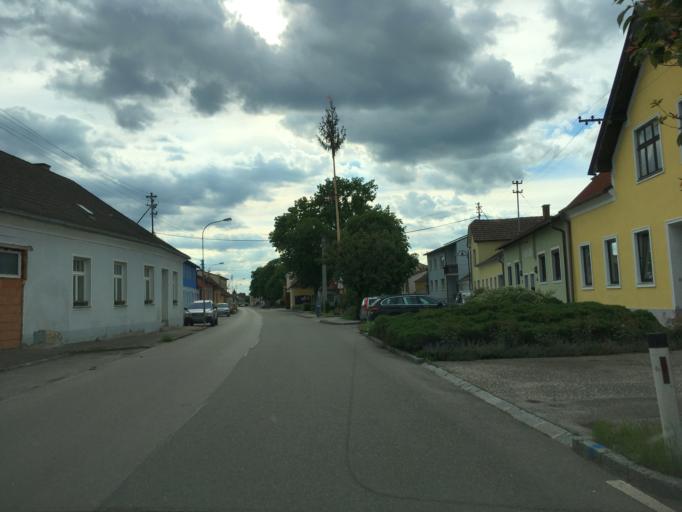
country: AT
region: Lower Austria
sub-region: Politischer Bezirk Tulln
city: Kirchberg am Wagram
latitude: 48.4076
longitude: 15.8924
